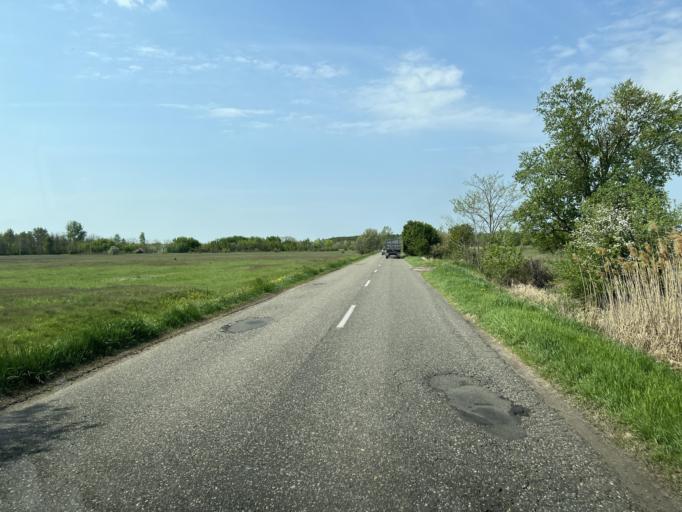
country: HU
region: Pest
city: Tortel
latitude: 47.0938
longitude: 19.8928
